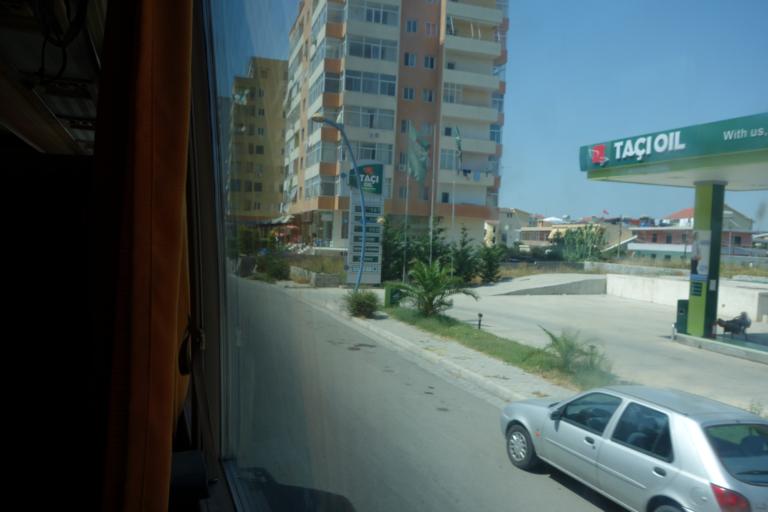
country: AL
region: Durres
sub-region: Rrethi i Durresit
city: Rrashbull
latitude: 41.2991
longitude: 19.5027
